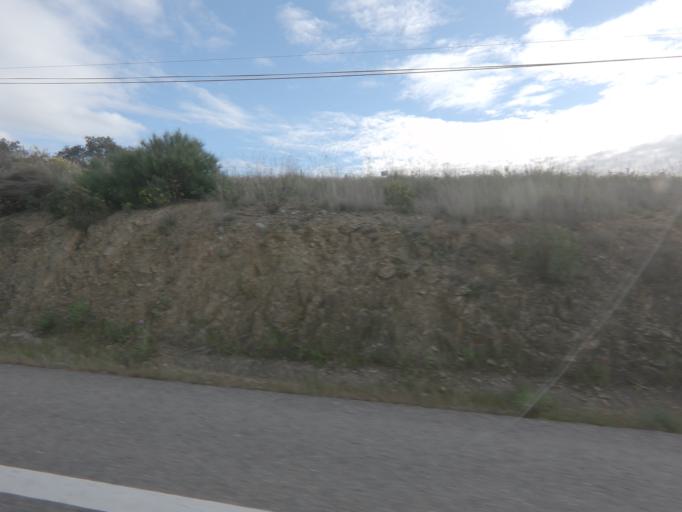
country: ES
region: Extremadura
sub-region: Provincia de Caceres
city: Canaveral
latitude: 39.8242
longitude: -6.3721
